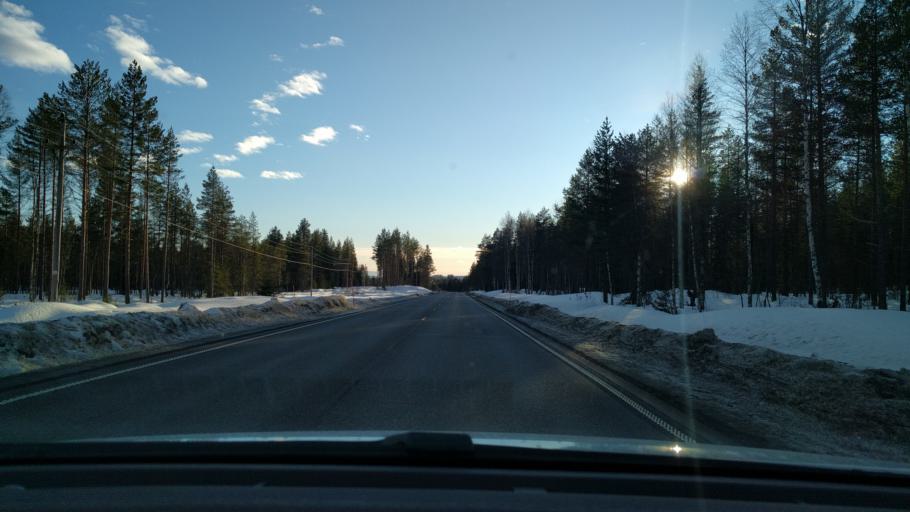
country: NO
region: Hedmark
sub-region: Elverum
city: Elverum
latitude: 61.0147
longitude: 11.8407
